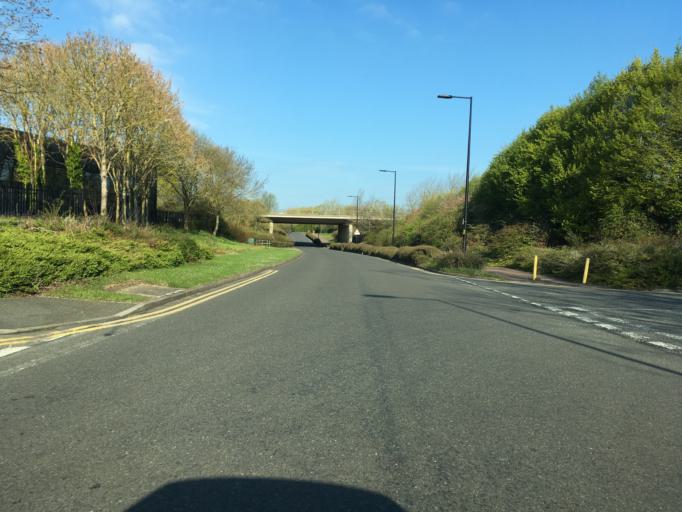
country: GB
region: England
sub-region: Milton Keynes
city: Newport Pagnell
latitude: 52.0690
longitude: -0.7317
